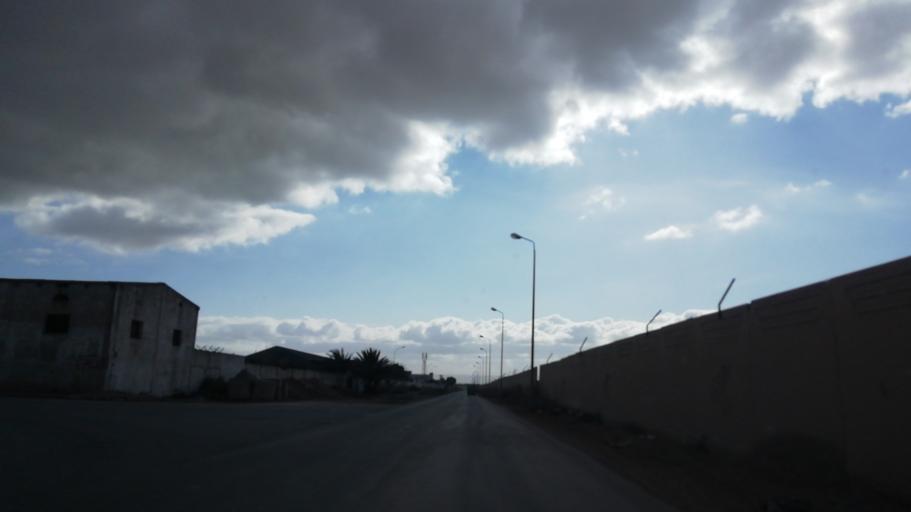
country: DZ
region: Oran
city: Es Senia
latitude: 35.6321
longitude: -0.5948
